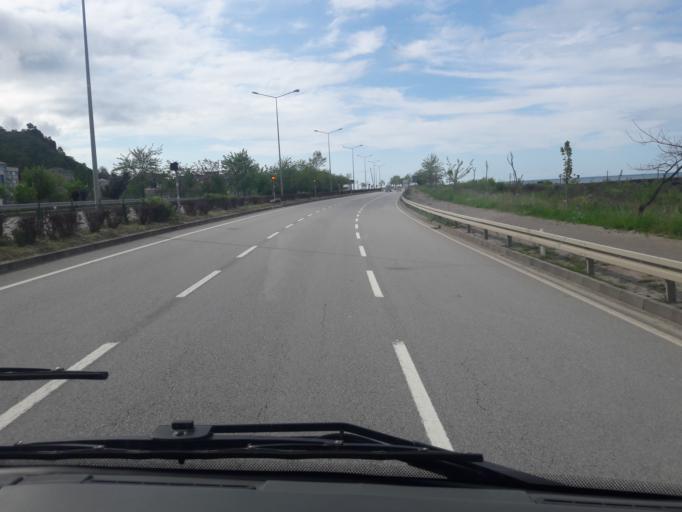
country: TR
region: Giresun
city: Piraziz
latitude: 40.9548
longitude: 38.1210
